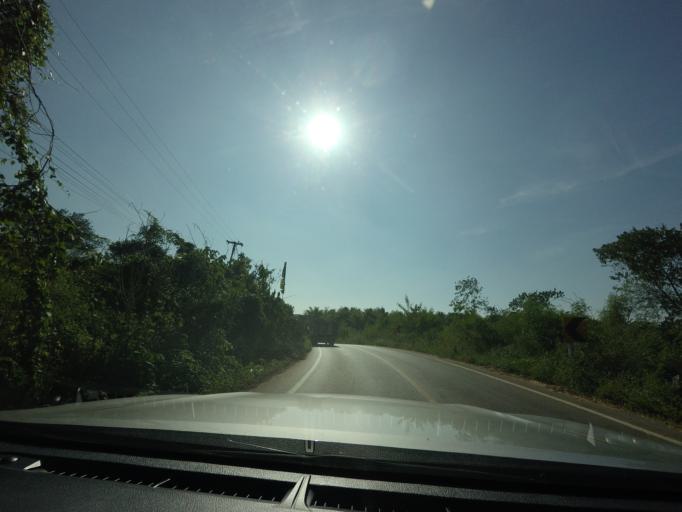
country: TH
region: Phrae
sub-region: Amphoe Wang Chin
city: Wang Chin
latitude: 17.7073
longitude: 99.6868
